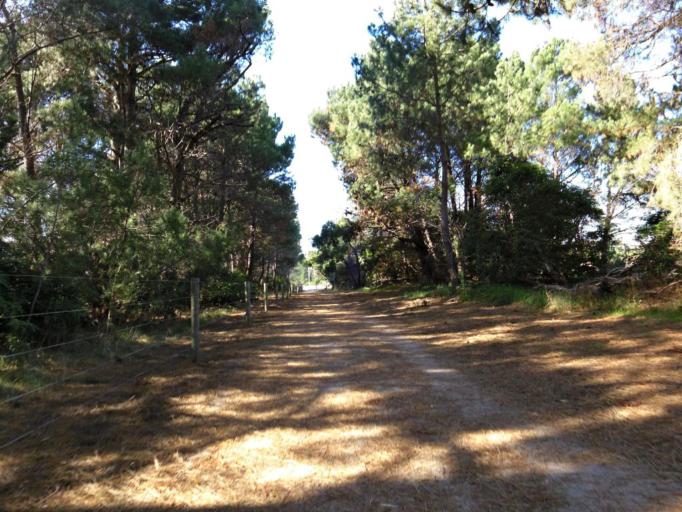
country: AU
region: Victoria
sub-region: Bass Coast
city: North Wonthaggi
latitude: -38.6031
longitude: 145.5768
